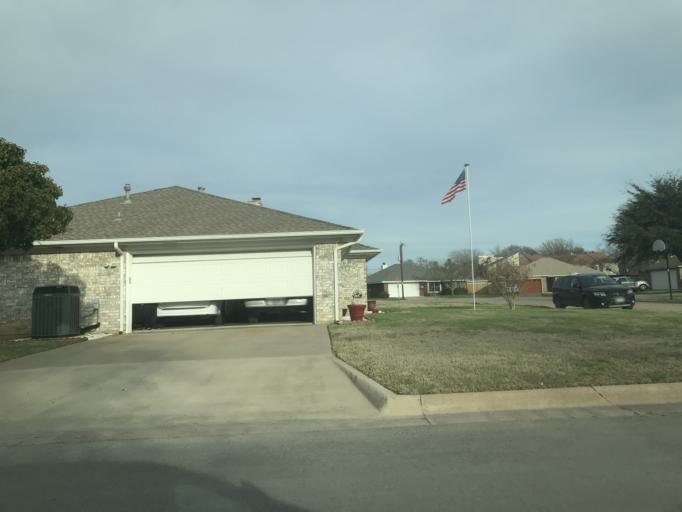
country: US
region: Texas
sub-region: Taylor County
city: Abilene
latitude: 32.3991
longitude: -99.7692
